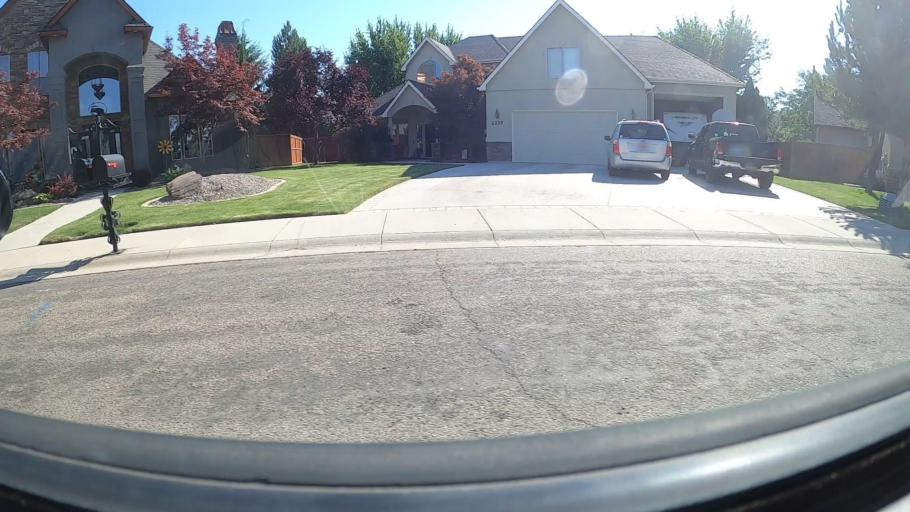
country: US
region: Idaho
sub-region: Ada County
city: Meridian
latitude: 43.6300
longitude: -116.3666
